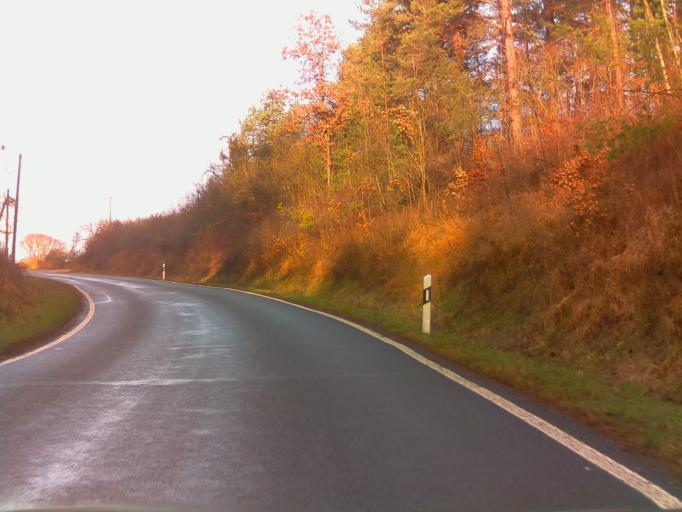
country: DE
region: Thuringia
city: Plaue
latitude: 50.8080
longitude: 10.9161
